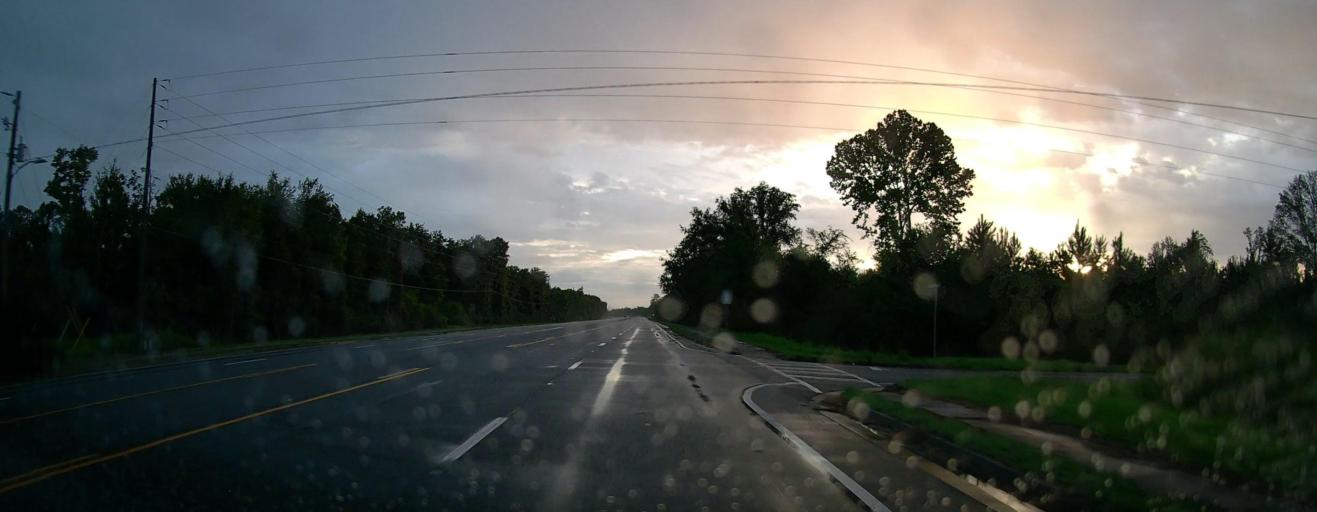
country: US
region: Georgia
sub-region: Clinch County
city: Homerville
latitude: 30.9881
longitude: -82.8733
